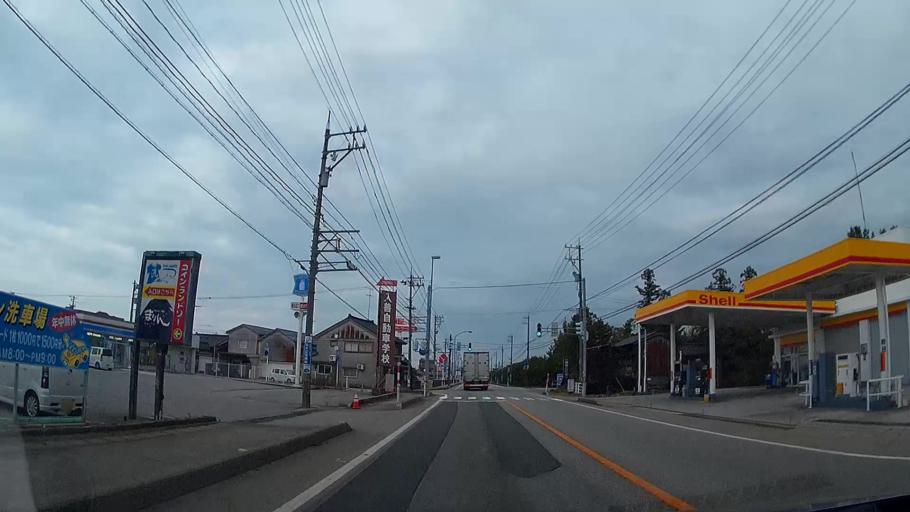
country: JP
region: Toyama
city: Nyuzen
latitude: 36.9303
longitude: 137.4993
